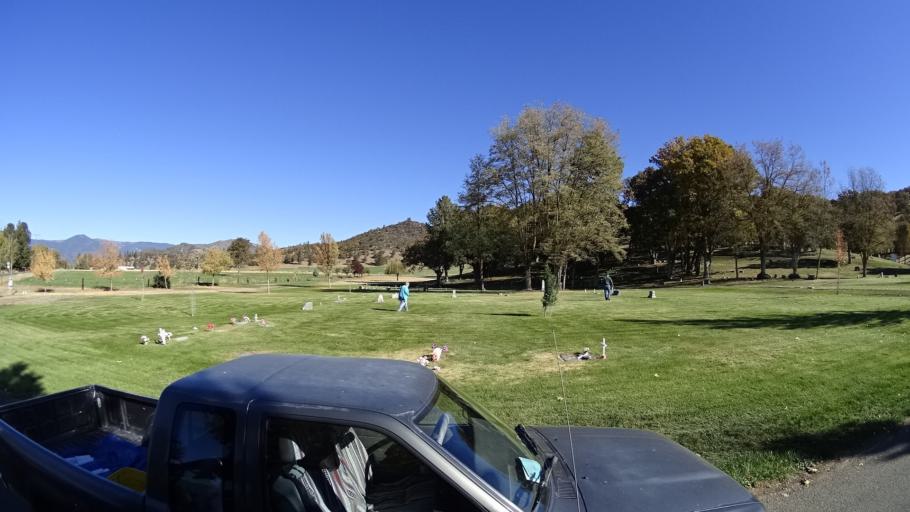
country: US
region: California
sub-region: Siskiyou County
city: Yreka
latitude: 41.5893
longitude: -122.8363
